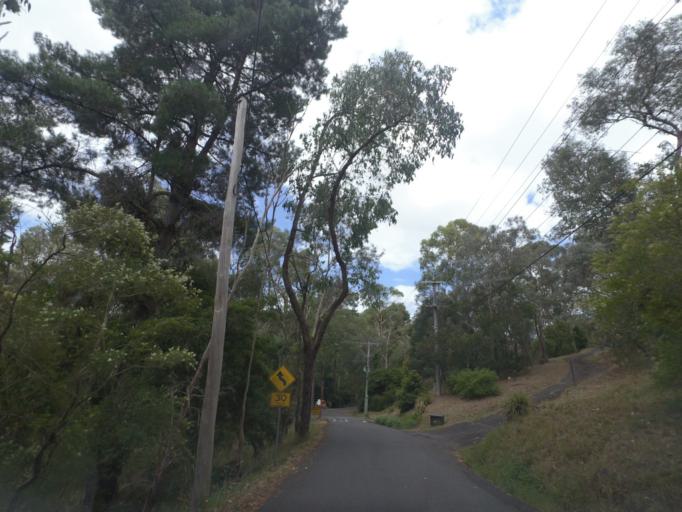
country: AU
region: Victoria
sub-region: Manningham
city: Park Orchards
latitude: -37.7921
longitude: 145.2134
